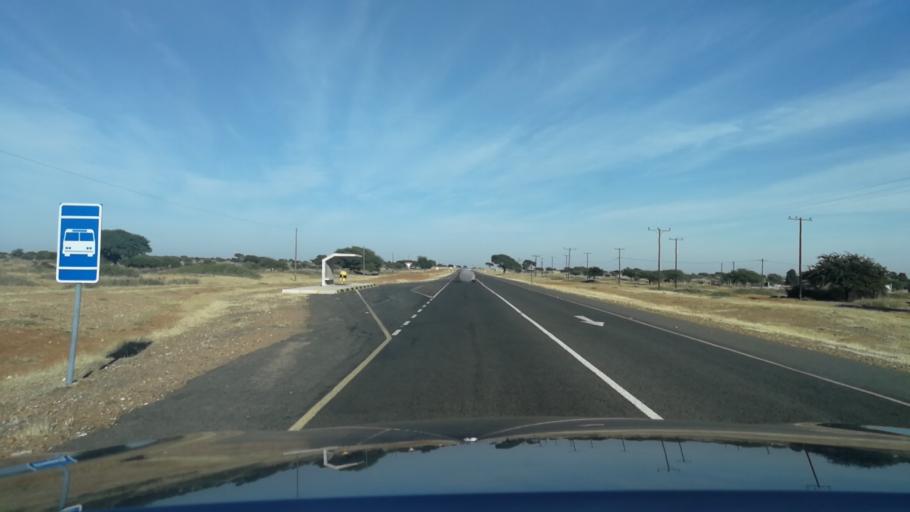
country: BW
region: South East
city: Janeng
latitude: -25.4691
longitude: 25.5374
